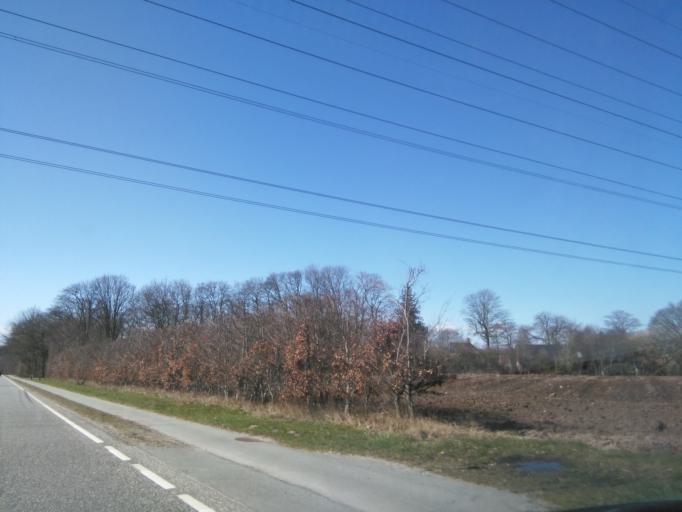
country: DK
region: Central Jutland
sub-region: Arhus Kommune
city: Kolt
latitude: 56.0986
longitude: 10.0560
